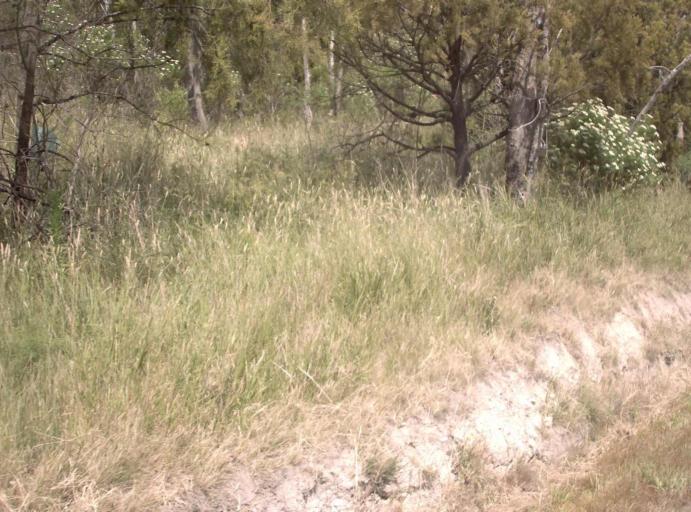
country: AU
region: Victoria
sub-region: Latrobe
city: Traralgon
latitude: -38.3026
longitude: 146.5392
